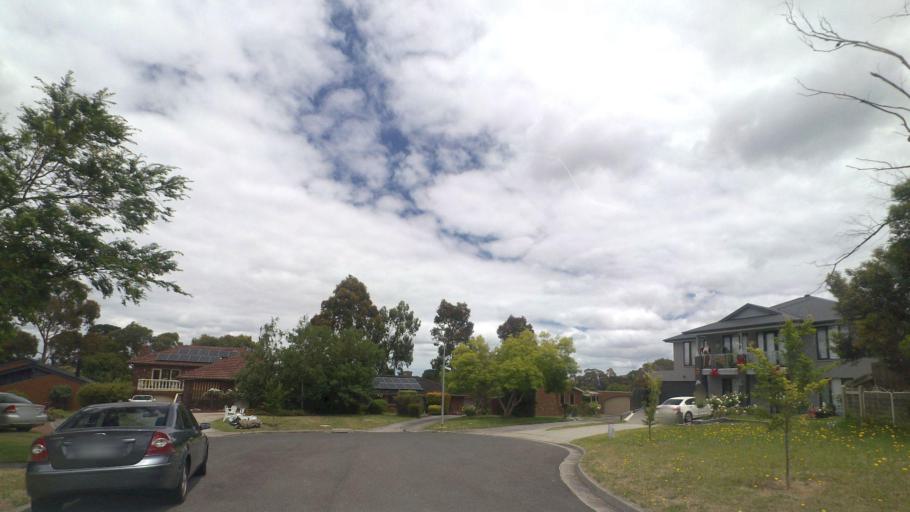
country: AU
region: Victoria
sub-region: Knox
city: Wantirna
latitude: -37.8540
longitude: 145.2310
